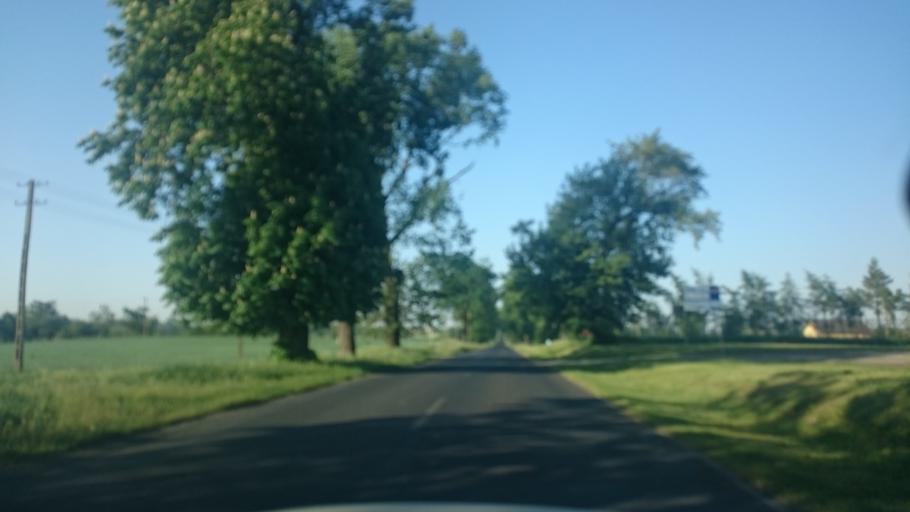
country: PL
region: Kujawsko-Pomorskie
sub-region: Powiat golubsko-dobrzynski
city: Zbojno
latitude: 52.9958
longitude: 19.1279
